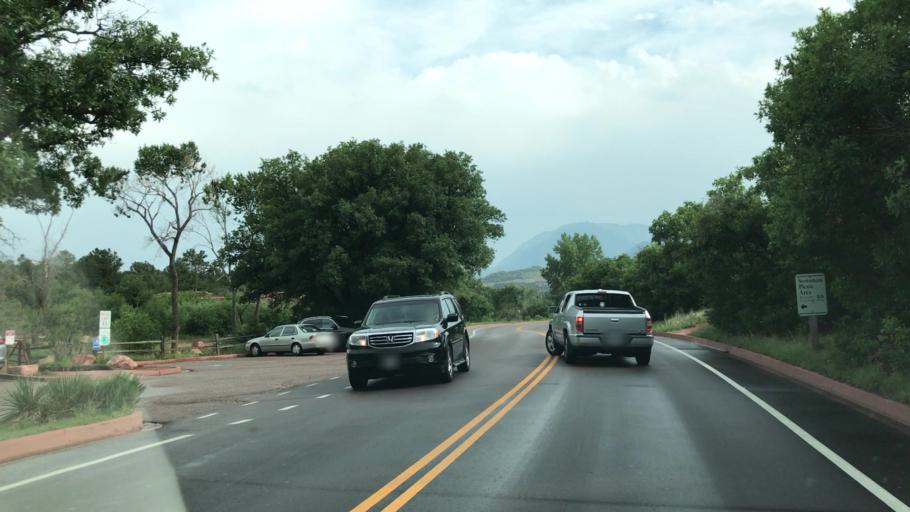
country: US
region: Colorado
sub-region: El Paso County
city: Manitou Springs
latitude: 38.8724
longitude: -104.8853
